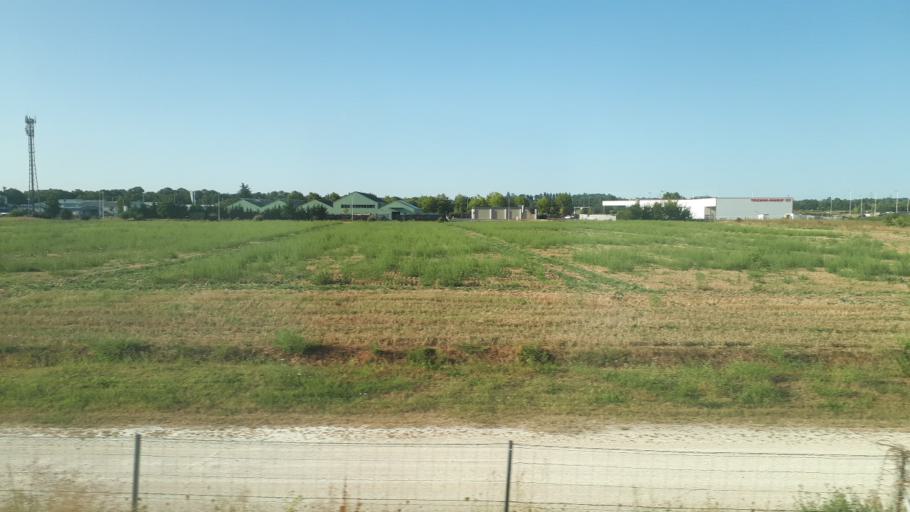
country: FR
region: Centre
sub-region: Departement d'Indre-et-Loire
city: La Ville-aux-Dames
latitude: 47.3903
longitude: 0.7867
